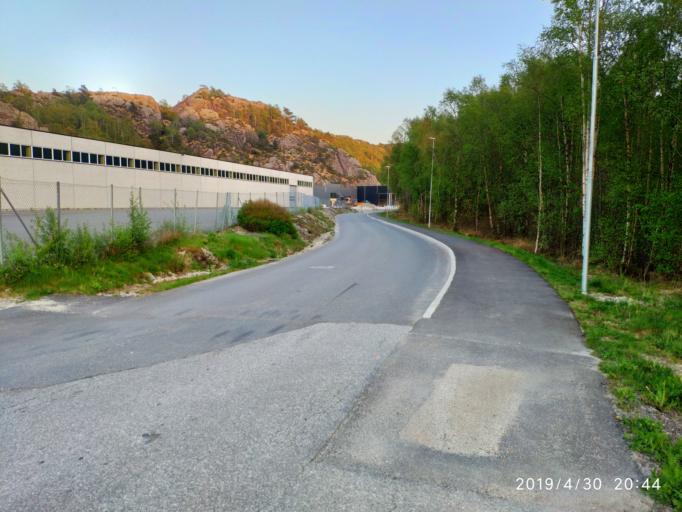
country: NO
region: Rogaland
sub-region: Eigersund
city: Egersund
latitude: 58.4782
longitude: 5.9982
